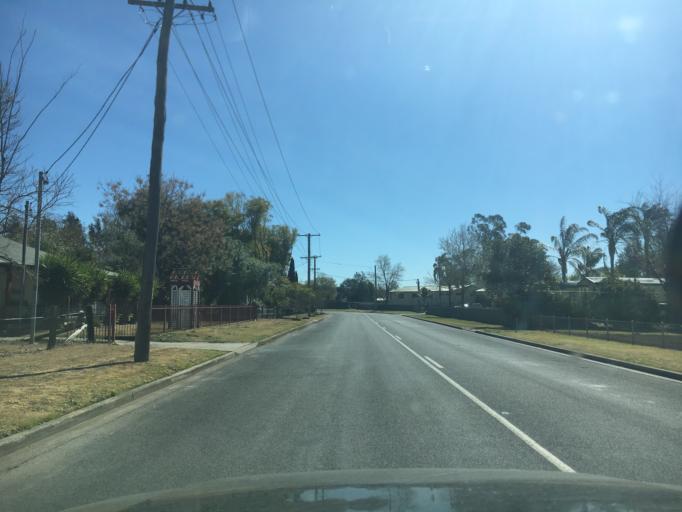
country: AU
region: New South Wales
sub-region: Singleton
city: Singleton
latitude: -32.5754
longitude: 151.1668
